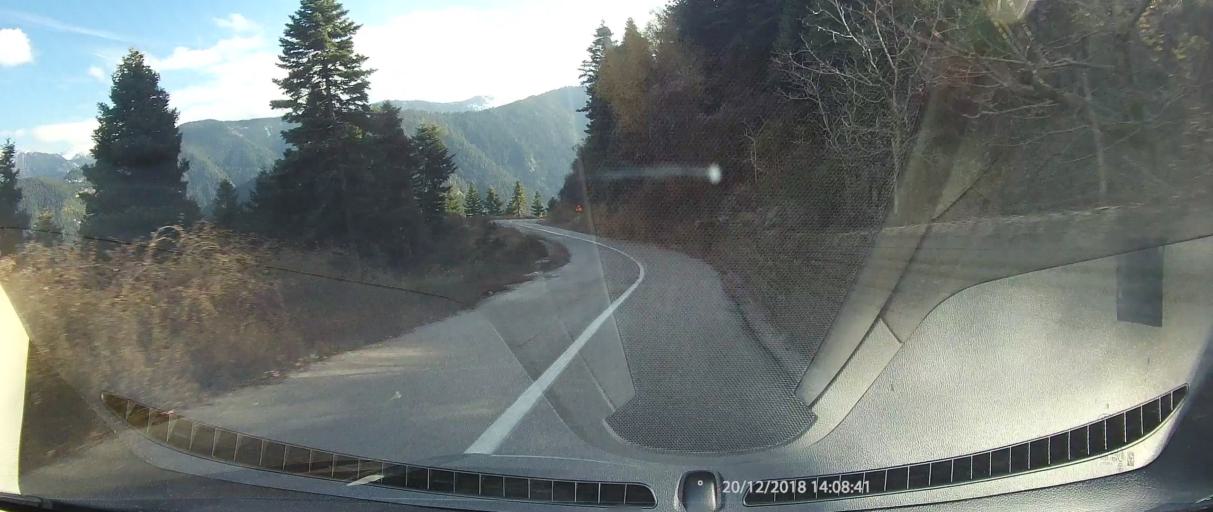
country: GR
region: West Greece
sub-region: Nomos Aitolias kai Akarnanias
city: Thermo
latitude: 38.7542
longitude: 21.6476
